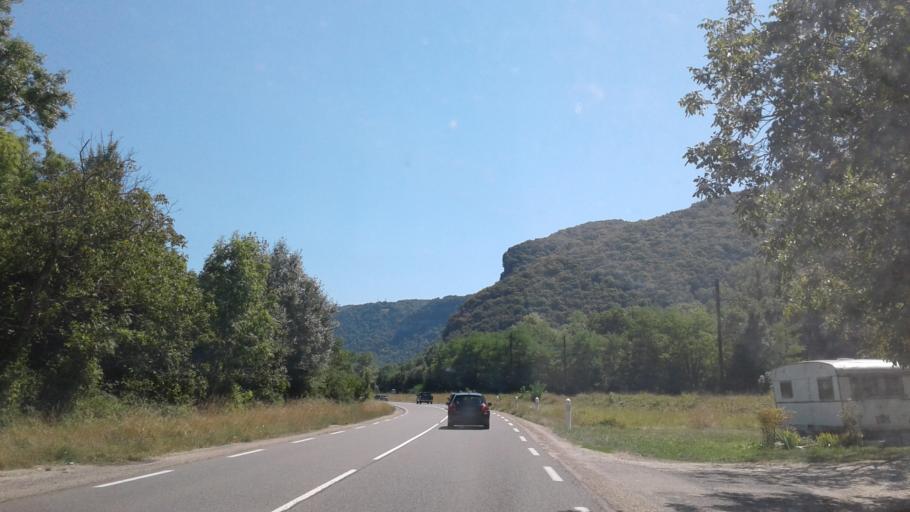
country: FR
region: Rhone-Alpes
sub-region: Departement de l'Ain
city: Vaux-en-Bugey
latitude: 45.9362
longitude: 5.3799
